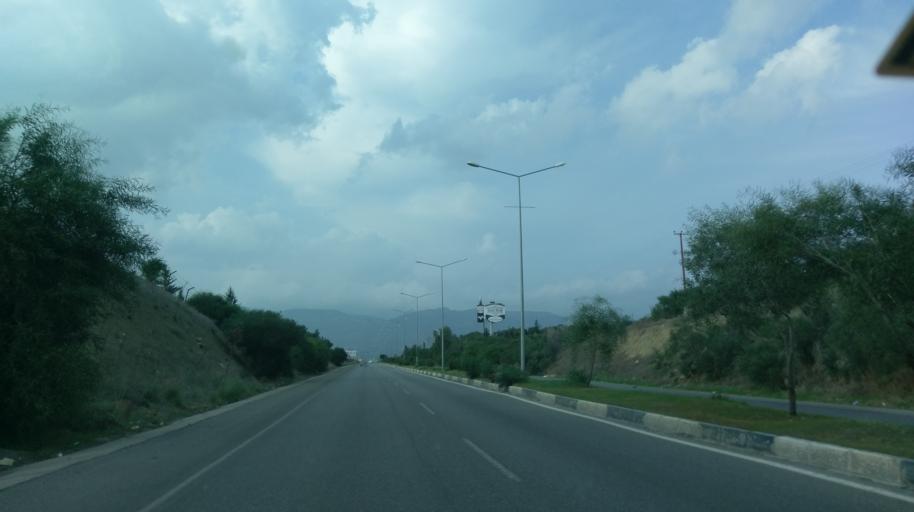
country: CY
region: Keryneia
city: Kyrenia
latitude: 35.2491
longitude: 33.3046
